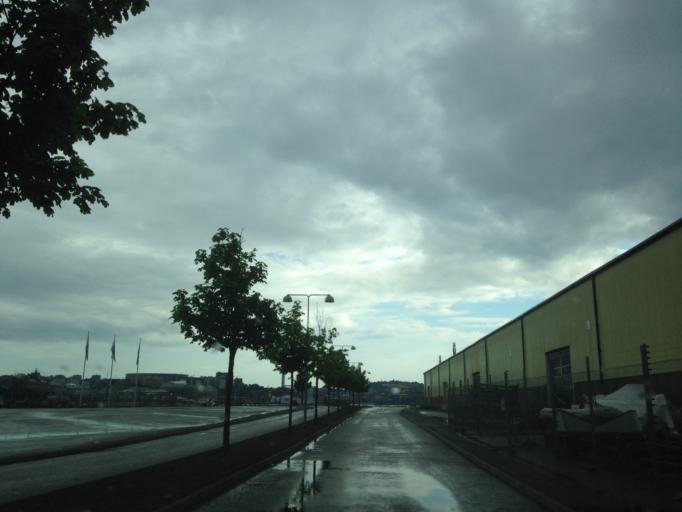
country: SE
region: Vaestra Goetaland
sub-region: Goteborg
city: Goeteborg
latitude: 57.7151
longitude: 11.9591
